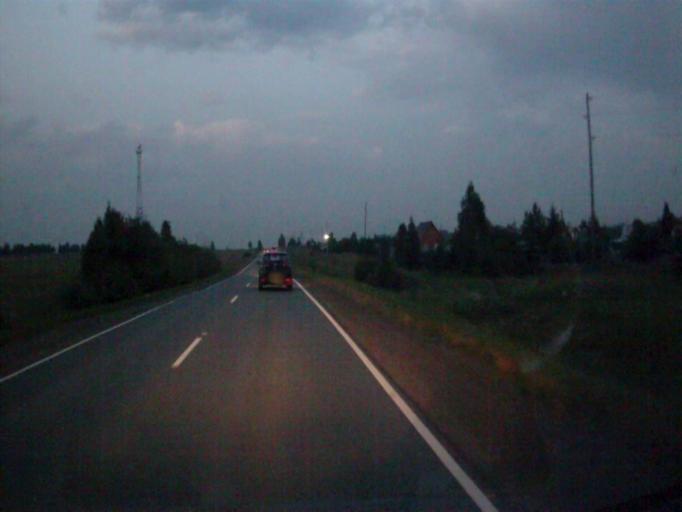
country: RU
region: Chelyabinsk
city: Poletayevo
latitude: 55.2109
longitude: 60.9133
